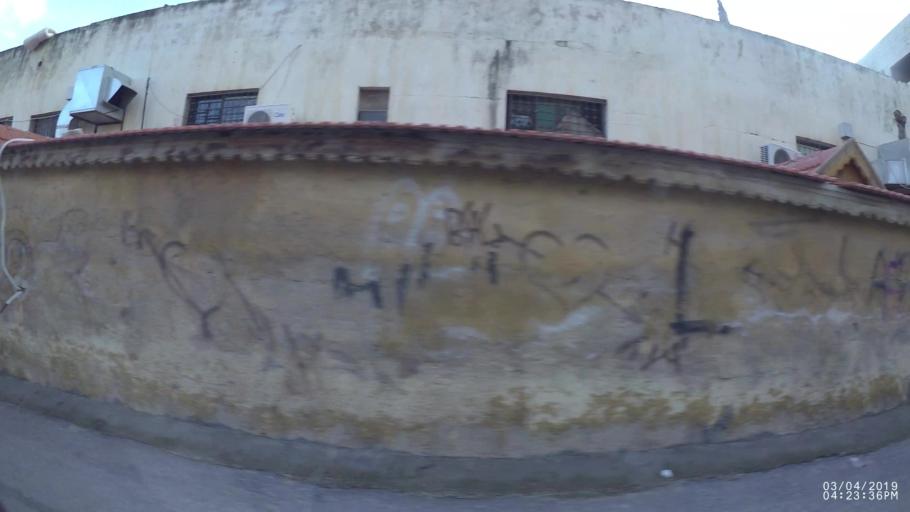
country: JO
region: Amman
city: Al Bunayyat ash Shamaliyah
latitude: 31.9104
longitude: 35.8901
